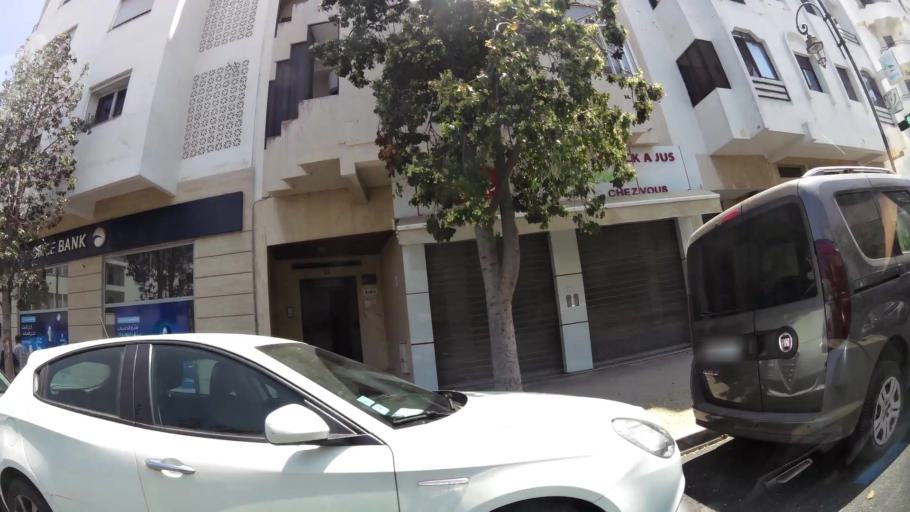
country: MA
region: Rabat-Sale-Zemmour-Zaer
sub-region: Rabat
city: Rabat
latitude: 34.0137
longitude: -6.8288
